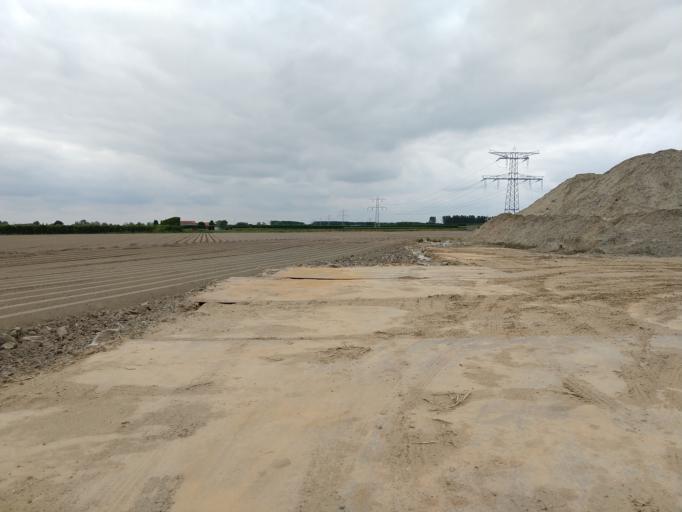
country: NL
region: Zeeland
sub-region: Gemeente Borsele
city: Borssele
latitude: 51.4468
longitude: 3.8104
